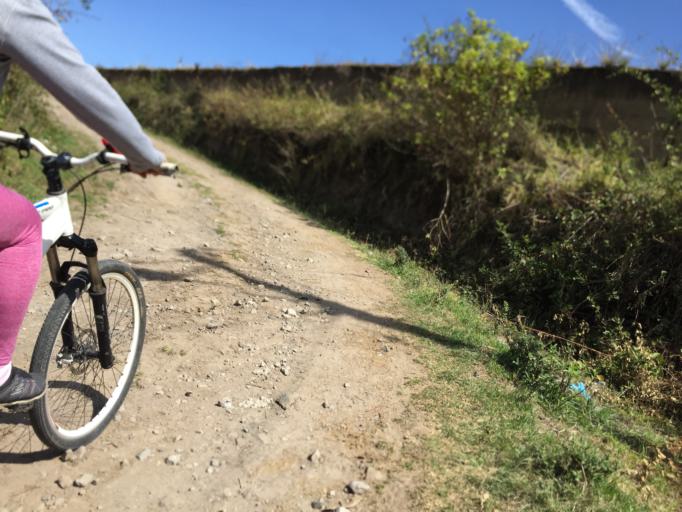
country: EC
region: Imbabura
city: Ibarra
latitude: 0.3113
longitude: -78.1573
